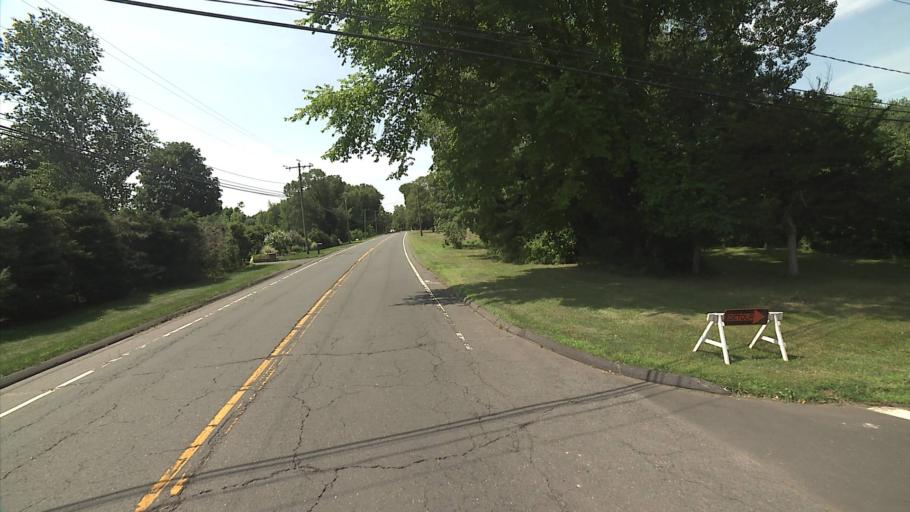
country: US
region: Connecticut
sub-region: New Haven County
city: Meriden
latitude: 41.5899
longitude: -72.8000
